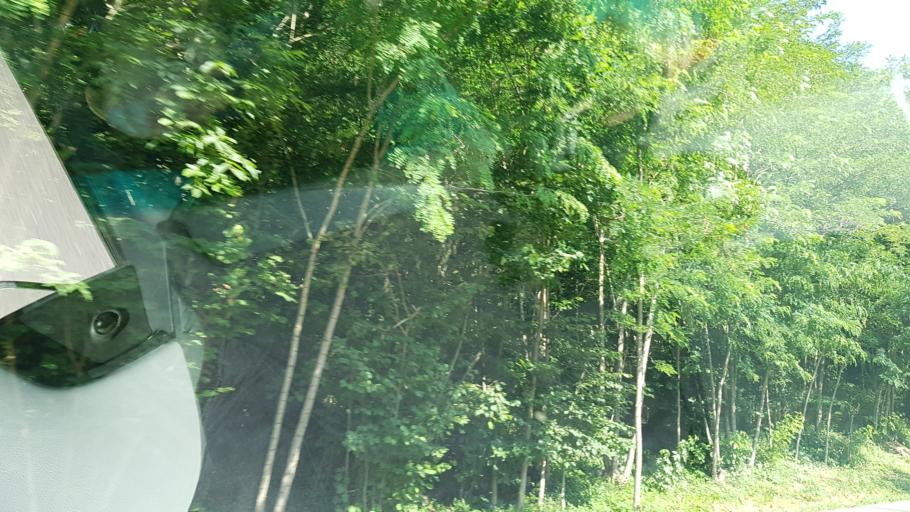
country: IT
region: Liguria
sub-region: Provincia di Genova
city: Serra Ricco
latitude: 44.5169
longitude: 8.9394
